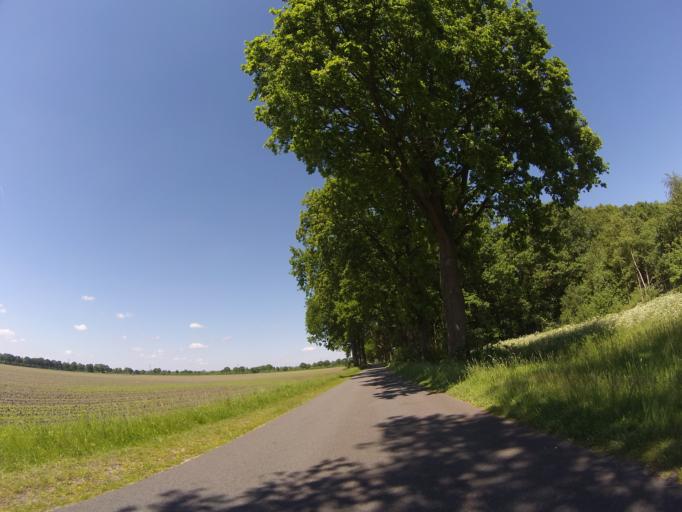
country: NL
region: Drenthe
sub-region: Gemeente Hoogeveen
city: Hoogeveen
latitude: 52.7782
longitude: 6.5145
